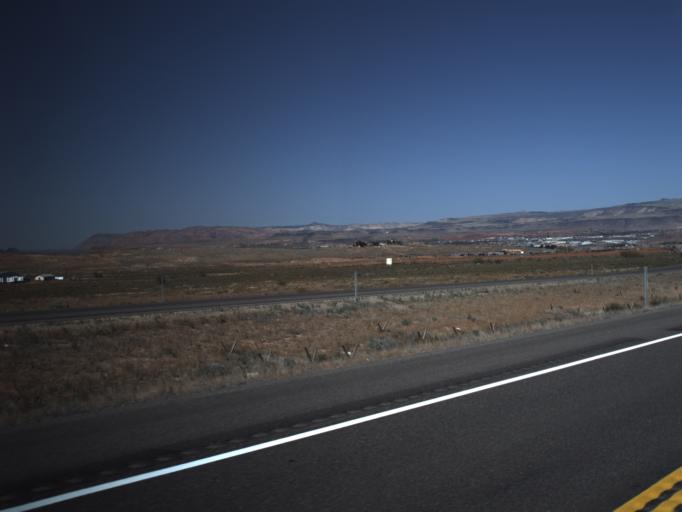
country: US
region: Utah
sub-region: Washington County
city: Washington
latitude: 37.0554
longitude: -113.4857
